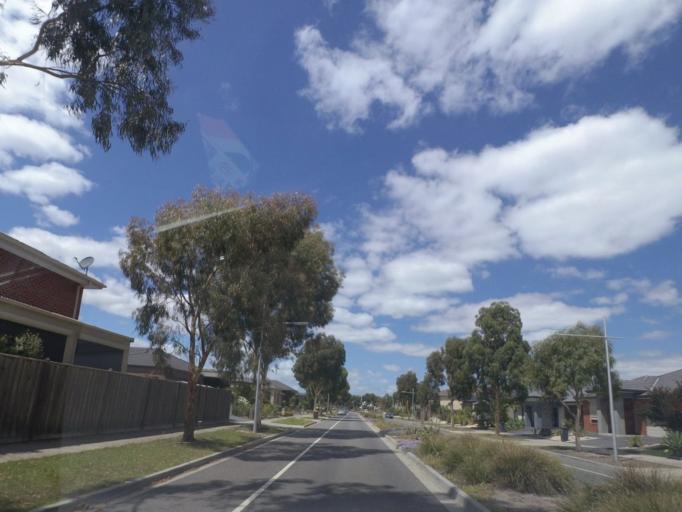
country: AU
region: Victoria
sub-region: Whittlesea
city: Lalor
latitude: -37.6596
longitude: 144.9970
